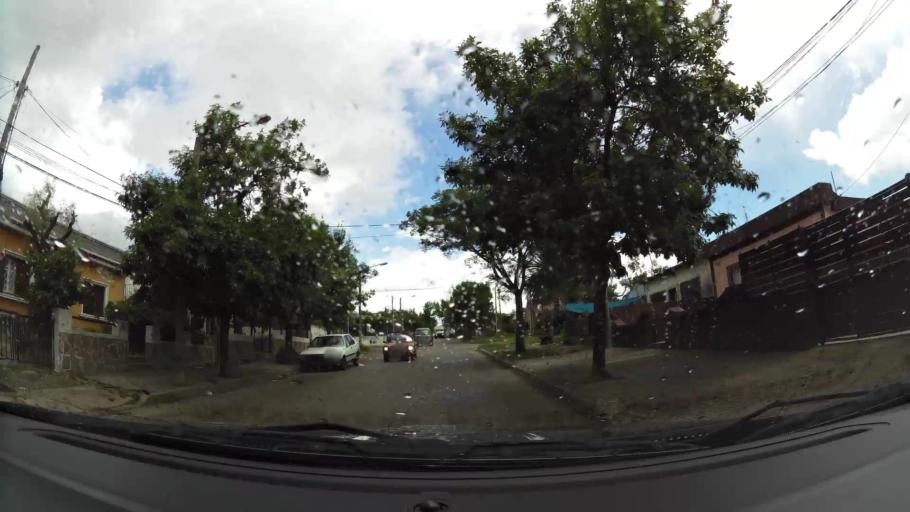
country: UY
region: Montevideo
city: Montevideo
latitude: -34.8506
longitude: -56.1663
